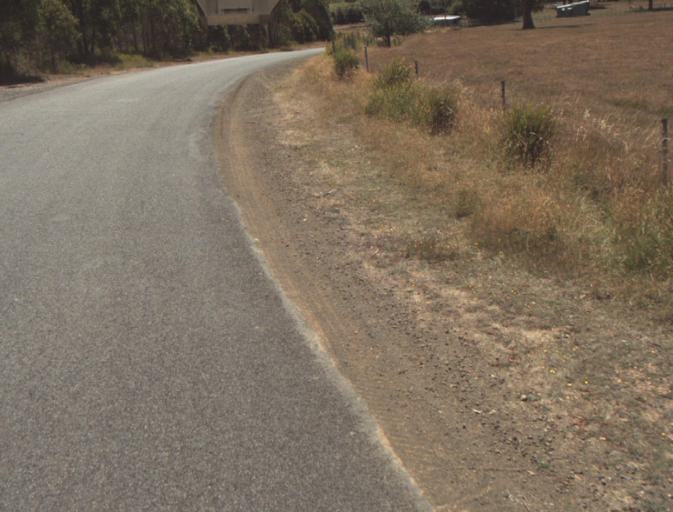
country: AU
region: Tasmania
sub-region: Dorset
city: Scottsdale
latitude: -41.3134
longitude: 147.3762
